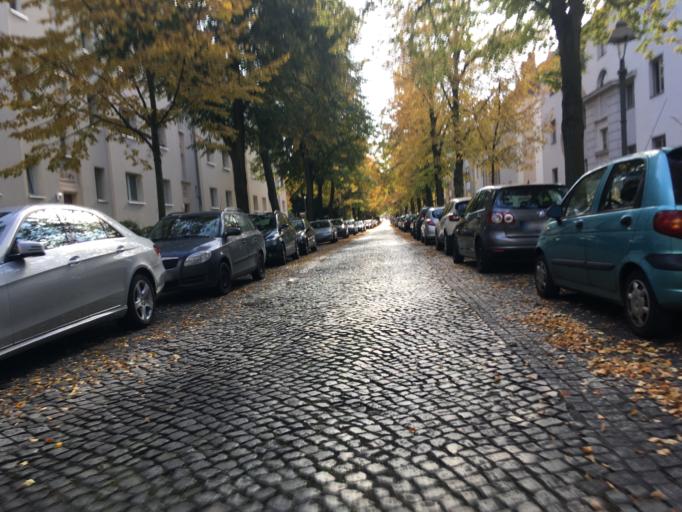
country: DE
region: Berlin
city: Wedding Bezirk
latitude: 52.5658
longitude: 13.3537
